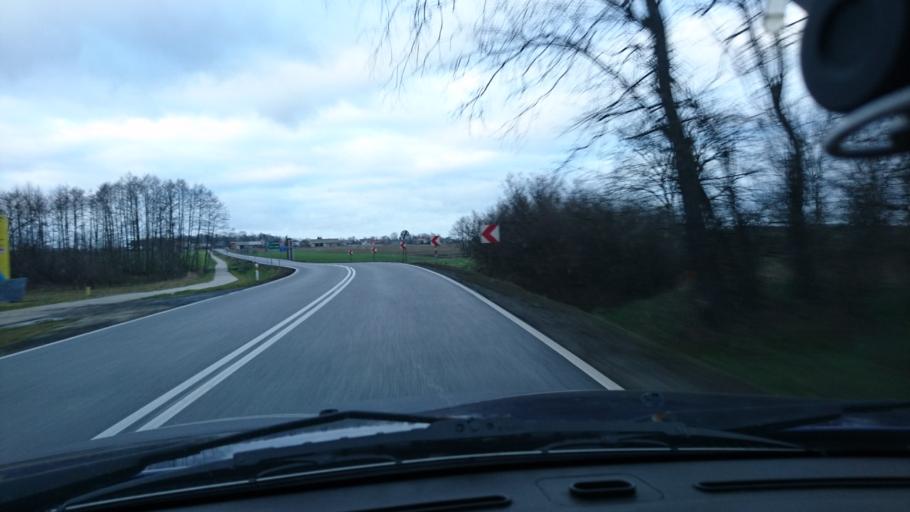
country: PL
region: Greater Poland Voivodeship
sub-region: Powiat kepinski
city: Opatow
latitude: 51.1700
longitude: 18.1466
